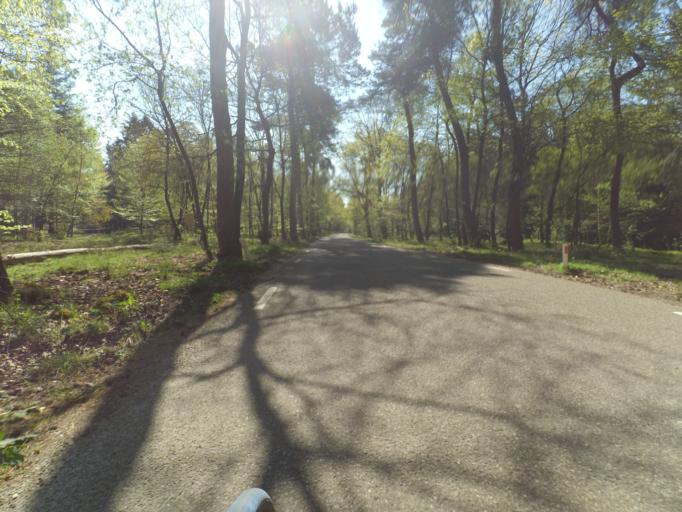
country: NL
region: Gelderland
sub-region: Gemeente Apeldoorn
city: Apeldoorn
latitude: 52.2244
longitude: 5.8774
